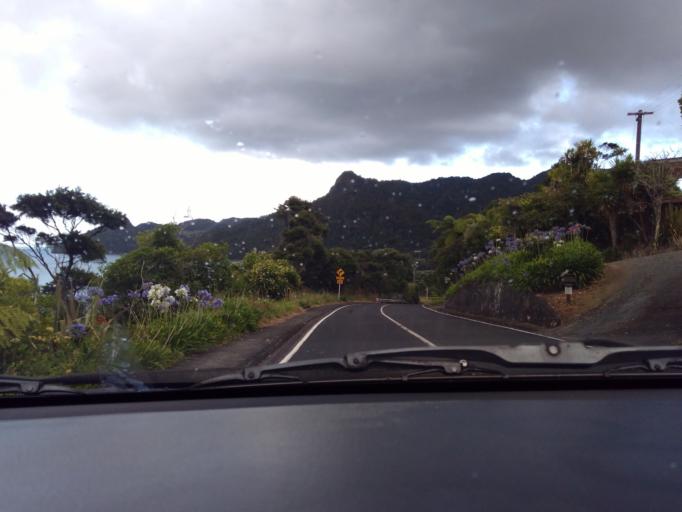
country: NZ
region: Auckland
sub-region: Auckland
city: Titirangi
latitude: -37.0032
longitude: 174.5739
